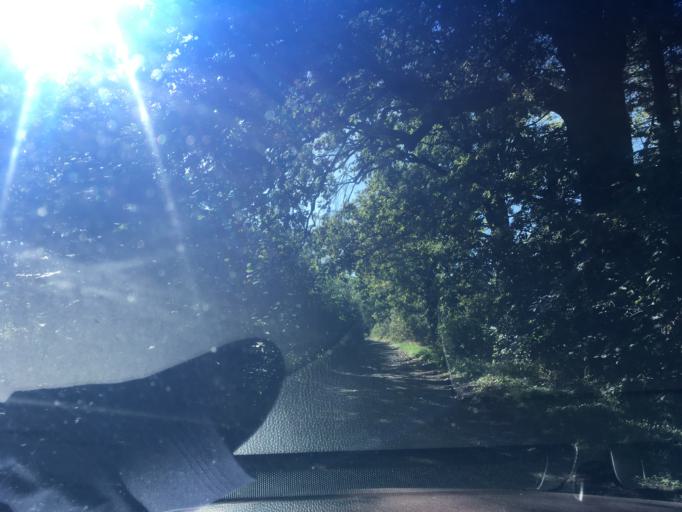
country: PL
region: Lower Silesian Voivodeship
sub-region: Powiat lubanski
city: Lesna
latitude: 51.0015
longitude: 15.1984
